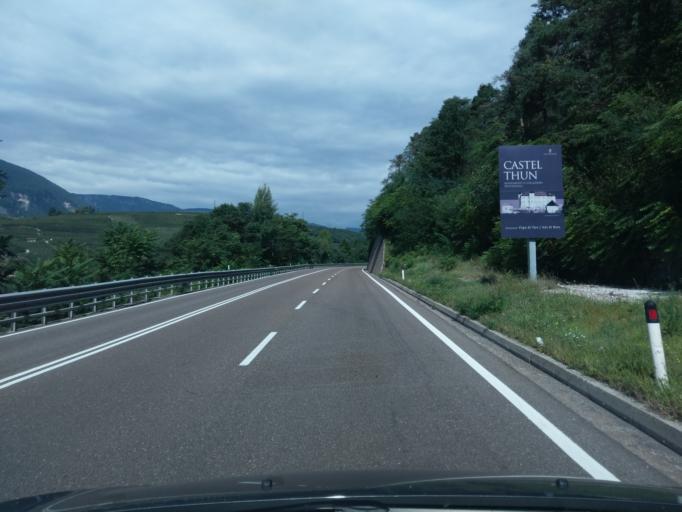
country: IT
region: Trentino-Alto Adige
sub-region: Provincia di Trento
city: Denno
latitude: 46.2799
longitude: 11.0634
